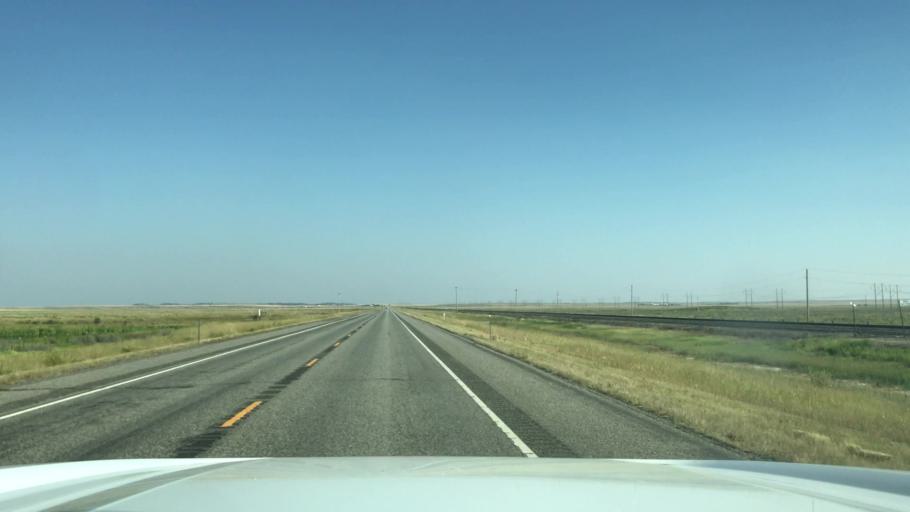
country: US
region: Montana
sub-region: Yellowstone County
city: Laurel
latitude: 45.9710
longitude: -108.7405
